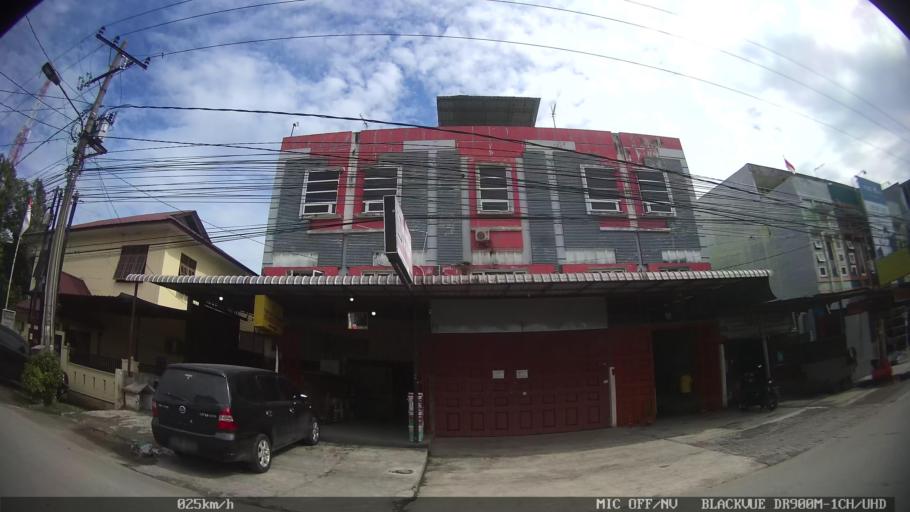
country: ID
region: North Sumatra
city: Sunggal
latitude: 3.6091
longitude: 98.6099
